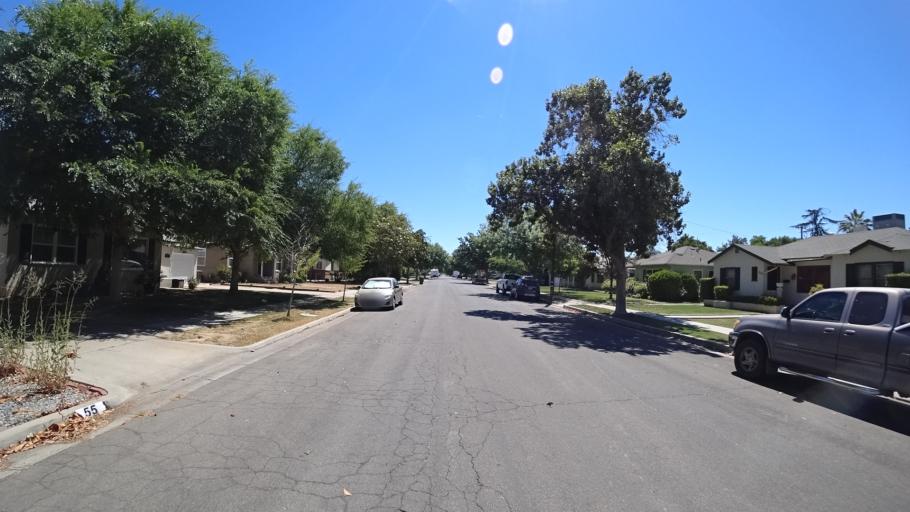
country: US
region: California
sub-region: Fresno County
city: Fresno
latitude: 36.7812
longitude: -119.8118
